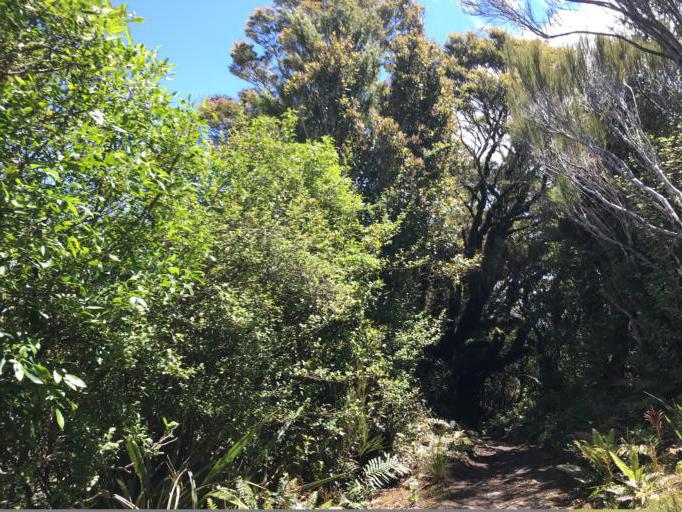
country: NZ
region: Wellington
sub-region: Kapiti Coast District
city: Otaki
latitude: -40.9085
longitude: 175.2574
